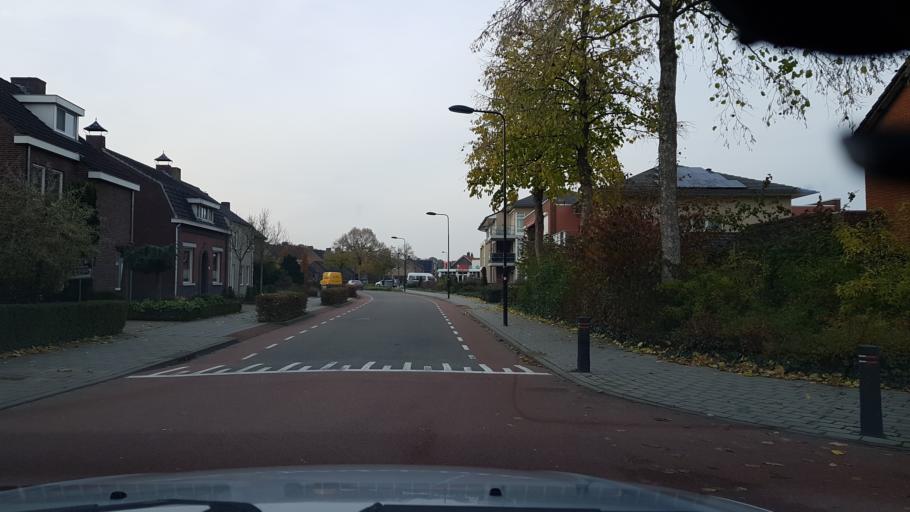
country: NL
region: Limburg
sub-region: Gemeente Beesel
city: Reuver
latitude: 51.2795
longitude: 6.0714
